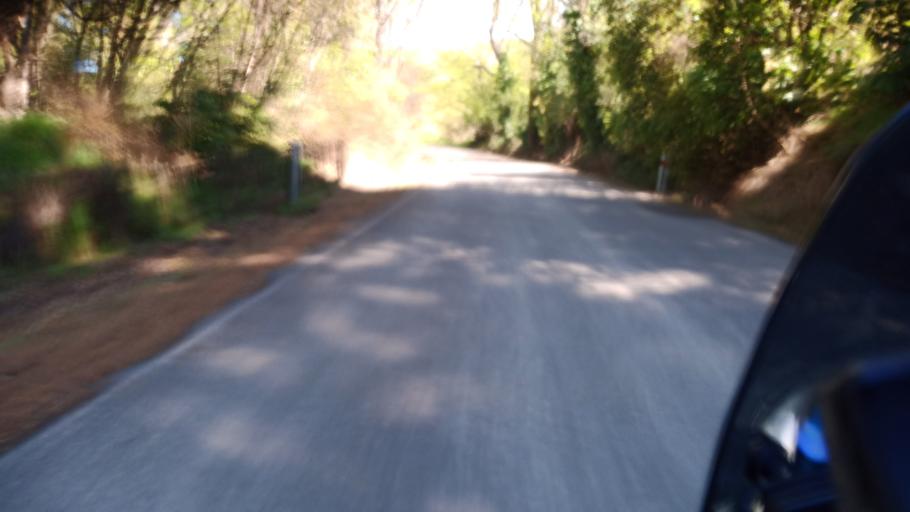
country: NZ
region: Gisborne
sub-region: Gisborne District
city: Gisborne
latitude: -38.7975
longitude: 177.7691
